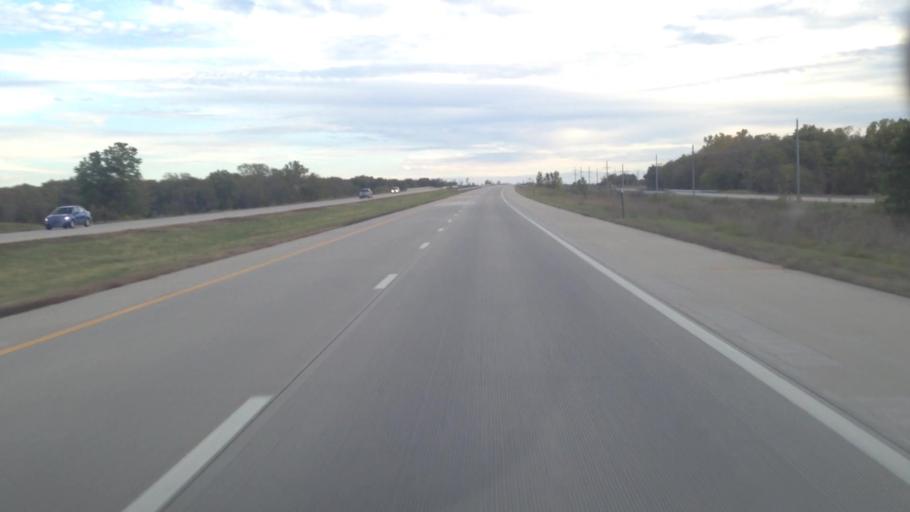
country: US
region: Kansas
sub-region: Douglas County
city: Baldwin City
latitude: 38.7441
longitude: -95.2677
